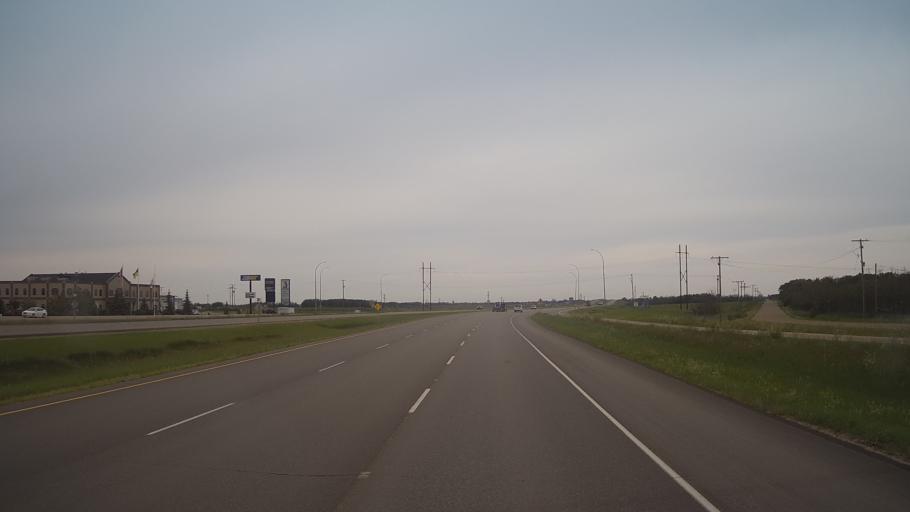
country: CA
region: Saskatchewan
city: Saskatoon
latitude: 52.0566
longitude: -106.5989
